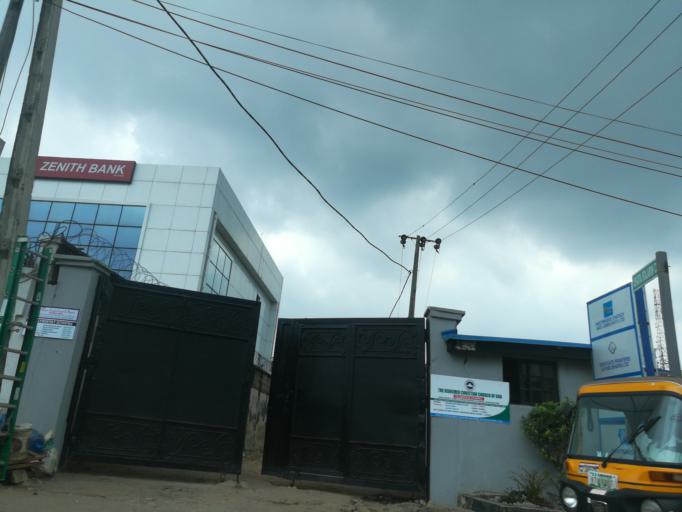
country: NG
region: Lagos
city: Ojota
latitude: 6.5899
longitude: 3.3753
